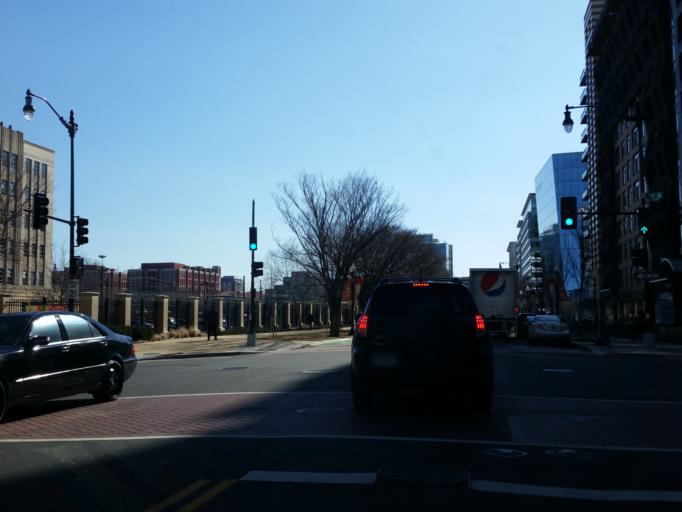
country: US
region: Washington, D.C.
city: Washington, D.C.
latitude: 38.9058
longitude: -77.0059
